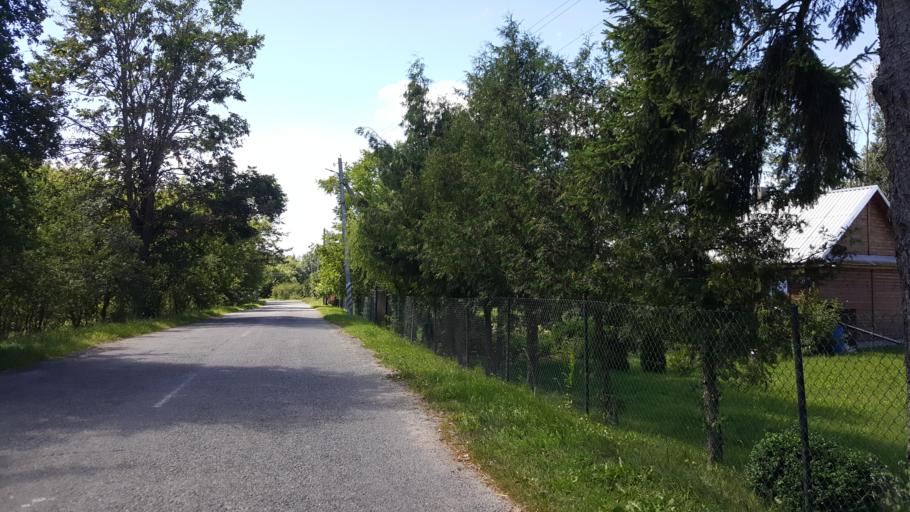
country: BY
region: Brest
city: Horad Kobryn
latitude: 52.2984
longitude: 24.3461
